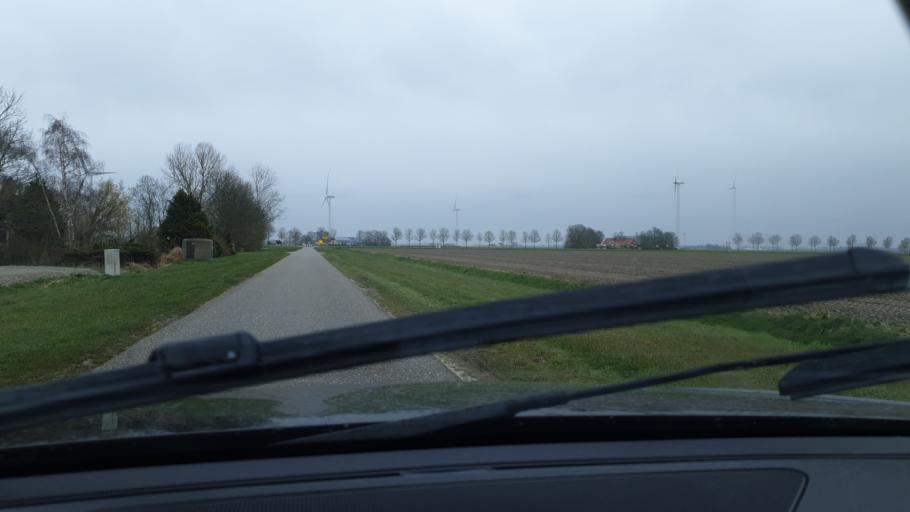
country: NL
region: Flevoland
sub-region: Gemeente Urk
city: Urk
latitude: 52.5621
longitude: 5.5771
